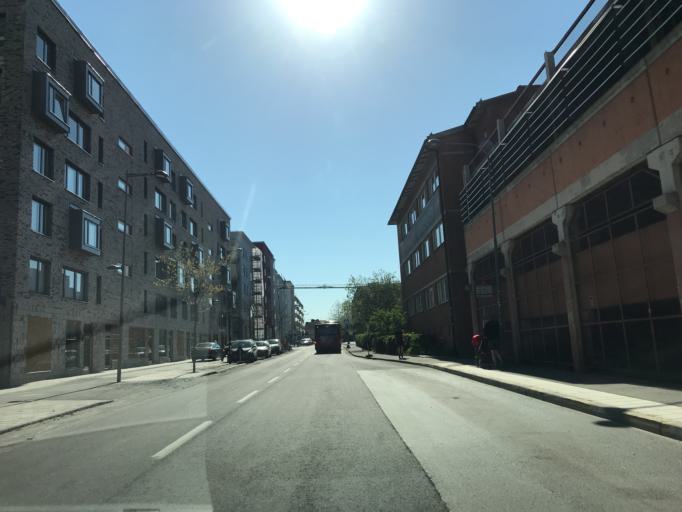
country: SE
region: Stockholm
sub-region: Stockholms Kommun
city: Arsta
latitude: 59.2805
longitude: 18.0132
